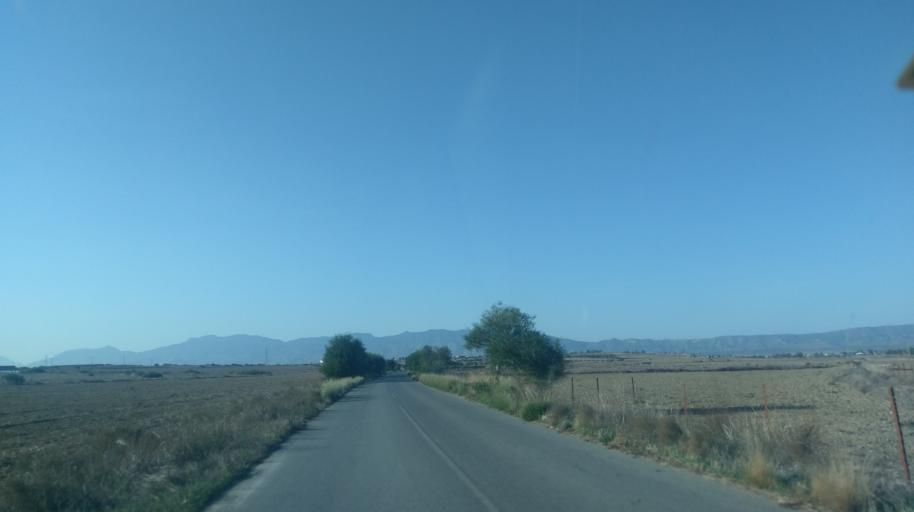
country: CY
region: Ammochostos
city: Lefkonoiko
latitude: 35.2268
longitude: 33.6928
